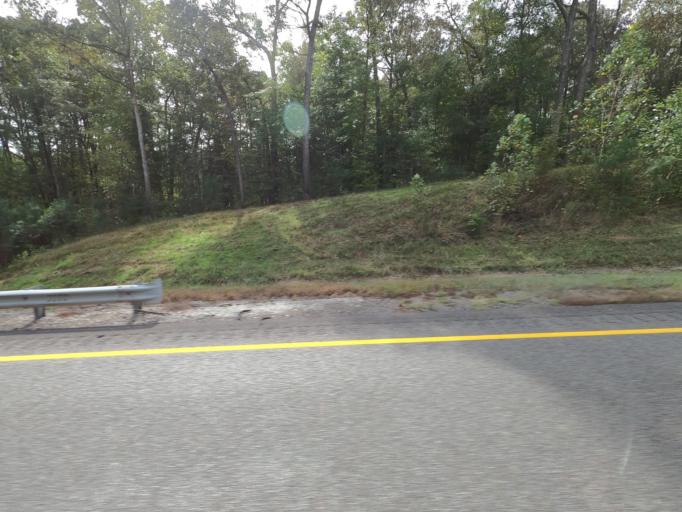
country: US
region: Tennessee
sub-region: Decatur County
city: Parsons
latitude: 35.8155
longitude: -88.2167
